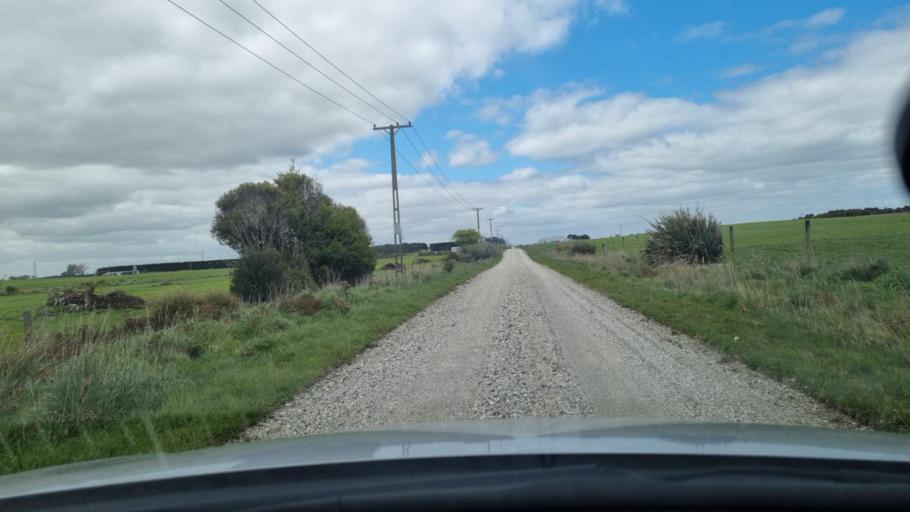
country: NZ
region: Southland
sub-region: Invercargill City
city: Invercargill
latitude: -46.4427
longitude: 168.4286
